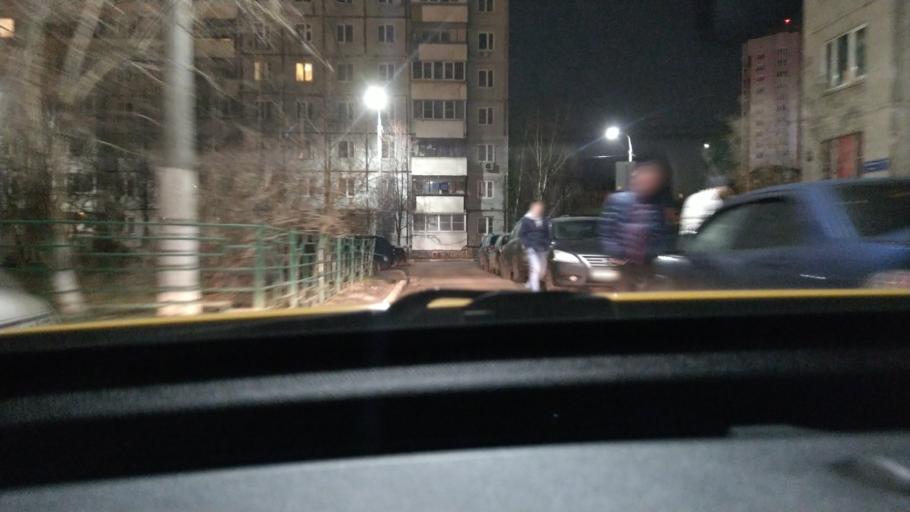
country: RU
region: Moskovskaya
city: Krasnogorsk
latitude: 55.8080
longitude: 37.3234
